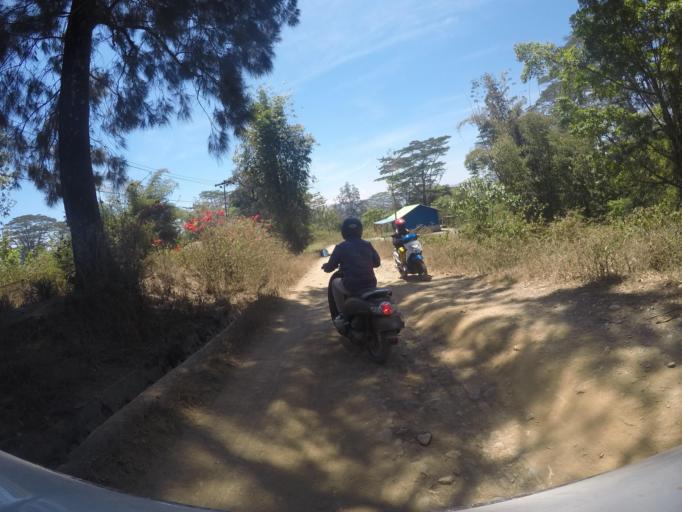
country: TL
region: Ermera
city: Gleno
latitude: -8.7327
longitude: 125.4134
